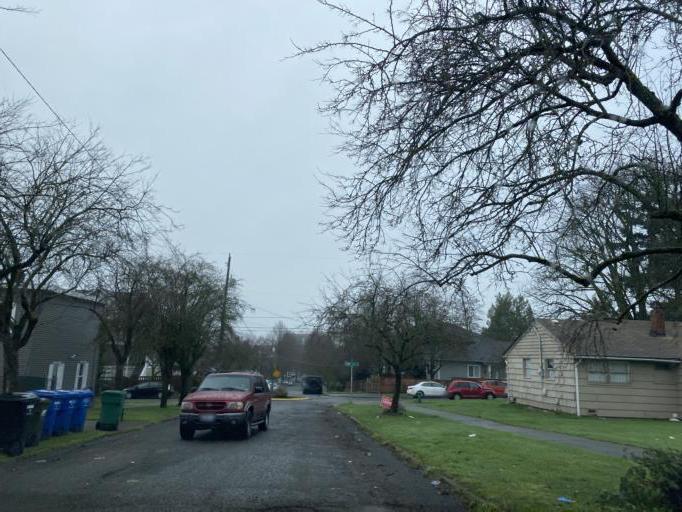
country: US
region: Washington
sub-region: King County
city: Seattle
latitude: 47.5980
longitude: -122.2956
